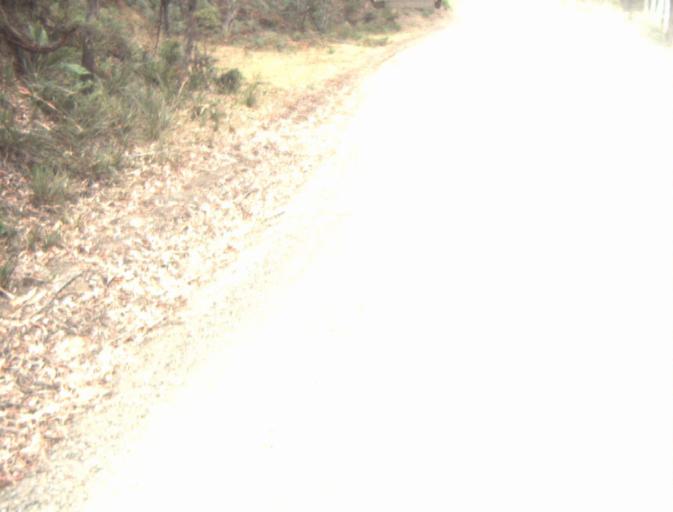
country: AU
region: Tasmania
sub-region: Northern Midlands
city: Evandale
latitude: -41.4550
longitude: 147.4827
